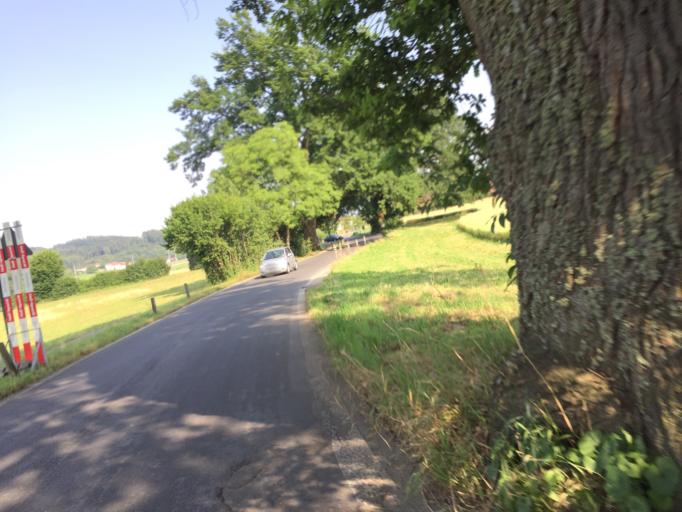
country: CH
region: Bern
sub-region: Bern-Mittelland District
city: Muri
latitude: 46.9438
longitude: 7.4805
